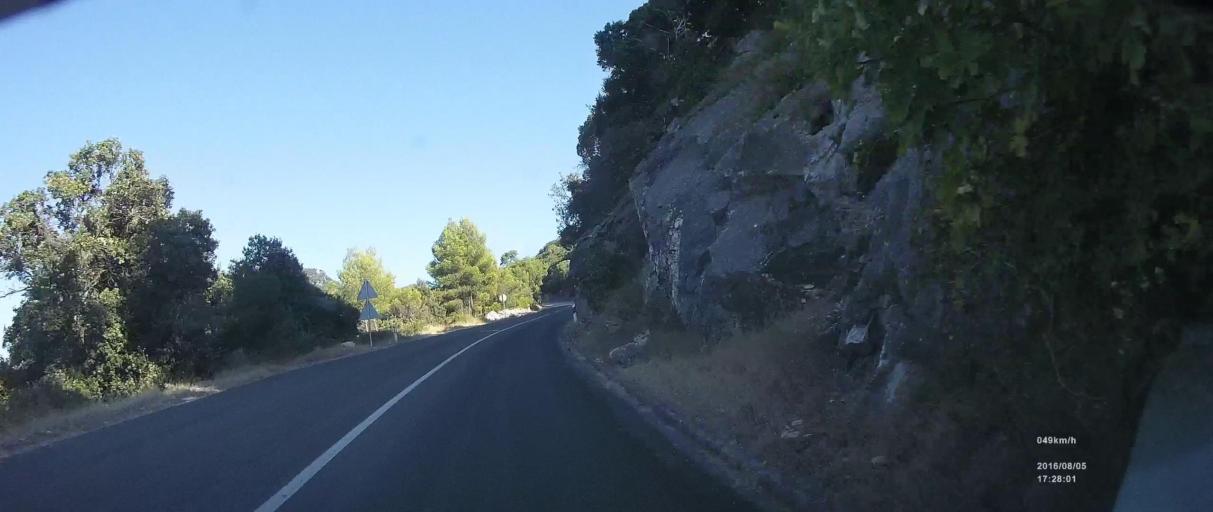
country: HR
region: Dubrovacko-Neretvanska
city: Blato
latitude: 42.7859
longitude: 17.4021
